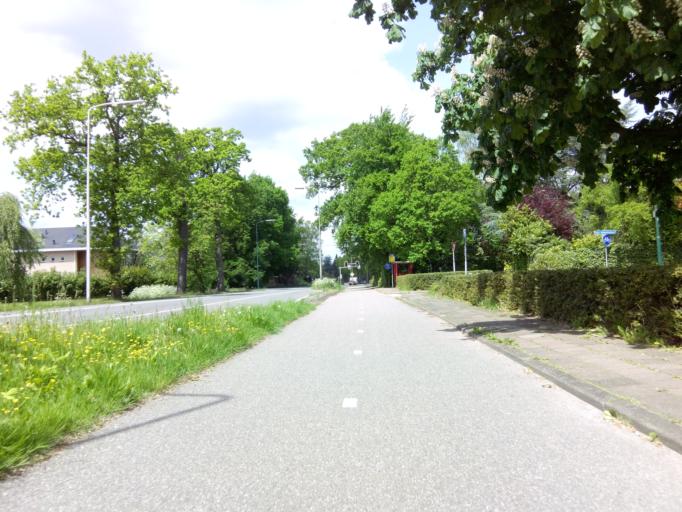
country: NL
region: Utrecht
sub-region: Gemeente Leusden
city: Leusden
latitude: 52.1127
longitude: 5.4056
